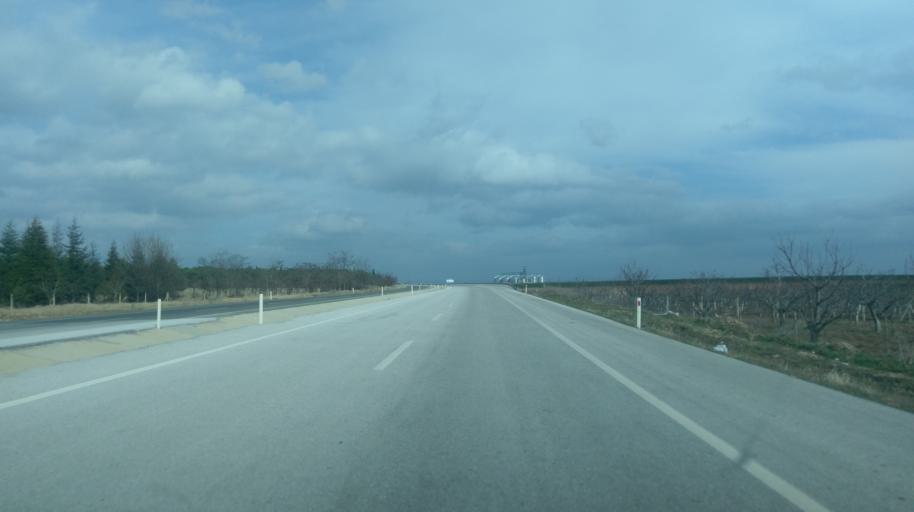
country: TR
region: Kirklareli
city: Kirklareli
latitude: 41.6983
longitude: 27.1520
